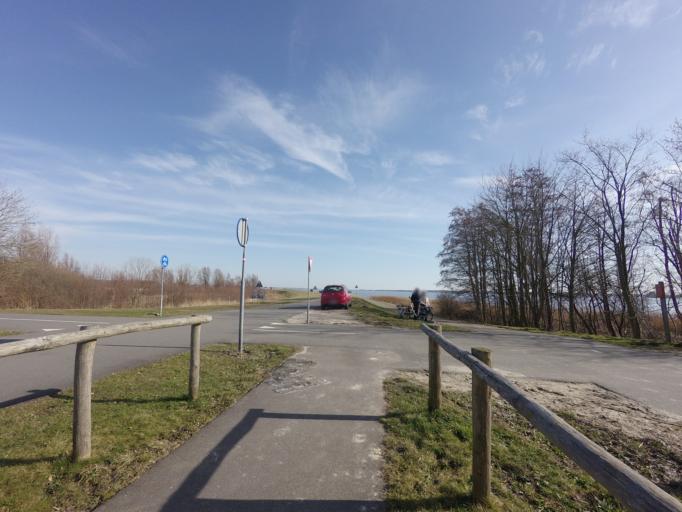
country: NL
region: North Holland
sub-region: Gemeente Naarden
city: Naarden
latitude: 52.3295
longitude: 5.1523
